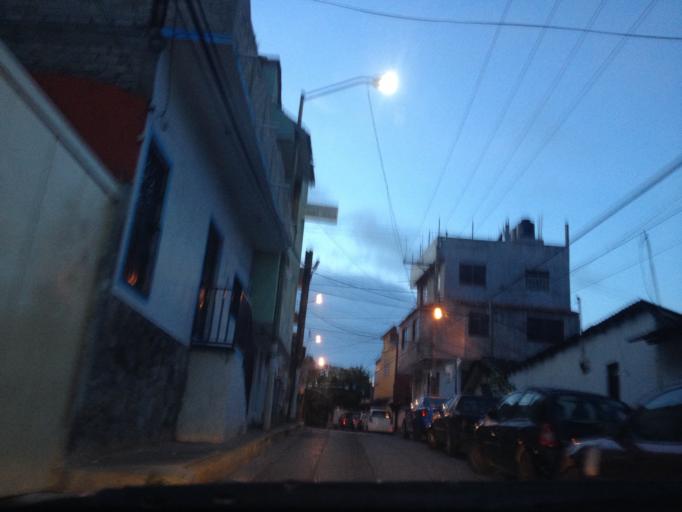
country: MX
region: Guerrero
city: Chilpancingo de los Bravos
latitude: 17.5581
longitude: -99.5015
